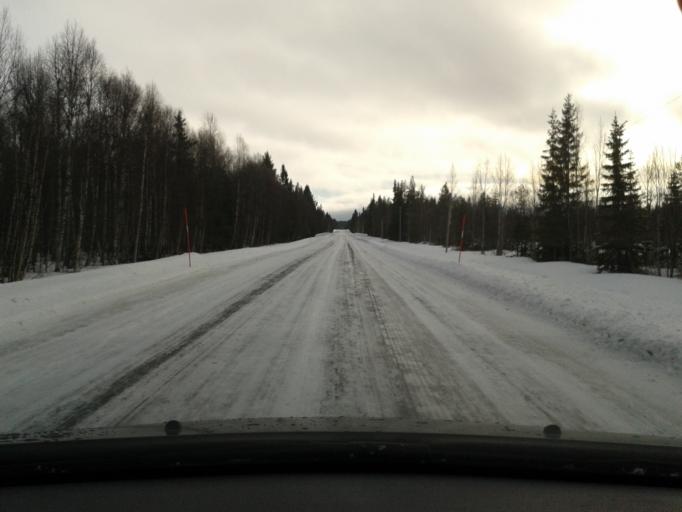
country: SE
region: Vaesterbotten
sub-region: Vilhelmina Kommun
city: Sjoberg
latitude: 64.7176
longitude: 16.2370
